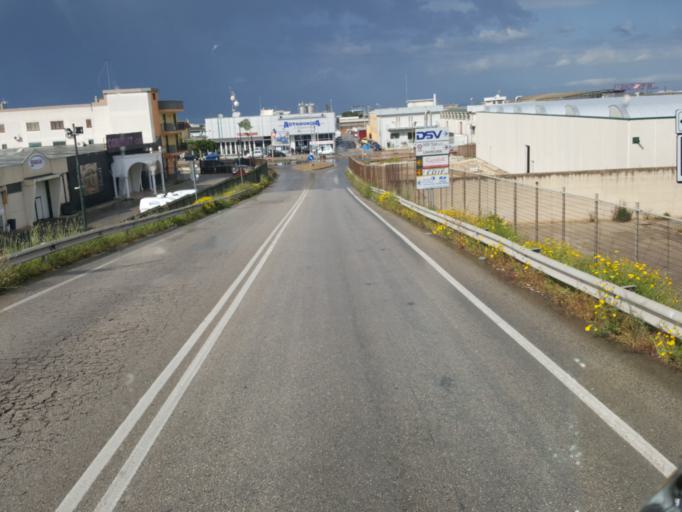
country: IT
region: Apulia
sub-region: Provincia di Barletta - Andria - Trani
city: Barletta
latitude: 41.3071
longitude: 16.3117
